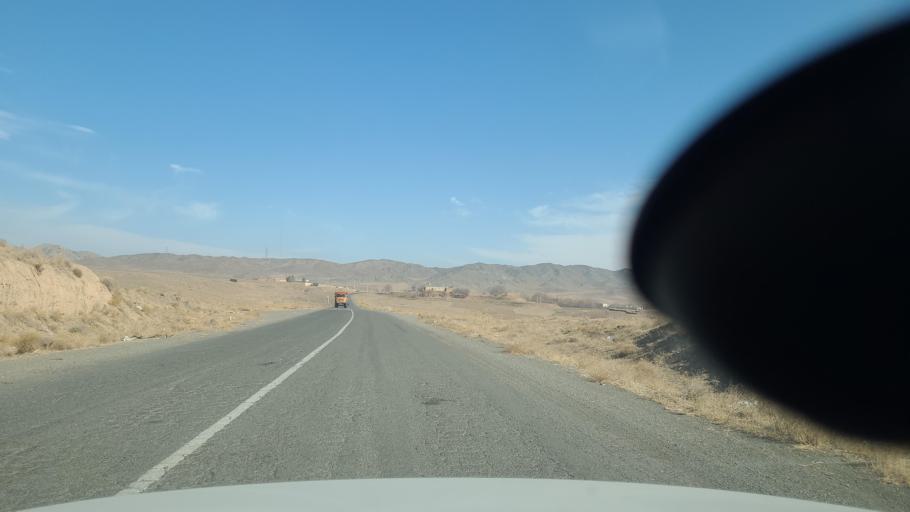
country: IR
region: Razavi Khorasan
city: Fariman
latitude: 35.5937
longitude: 59.6921
